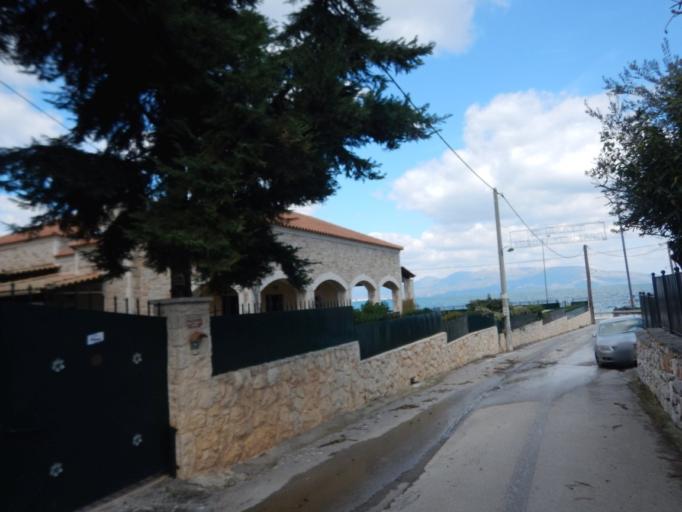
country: GR
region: Attica
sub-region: Nomarchia Anatolikis Attikis
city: Kalamos
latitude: 38.3070
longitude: 23.8543
